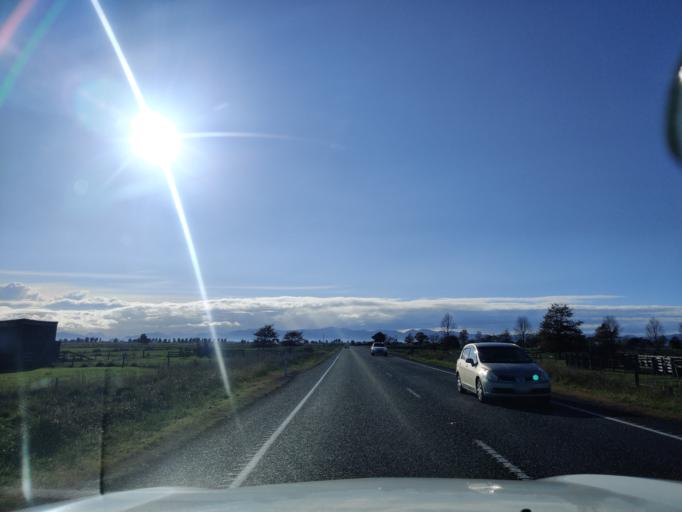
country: NZ
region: Waikato
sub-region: Hauraki District
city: Ngatea
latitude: -37.2778
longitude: 175.4595
